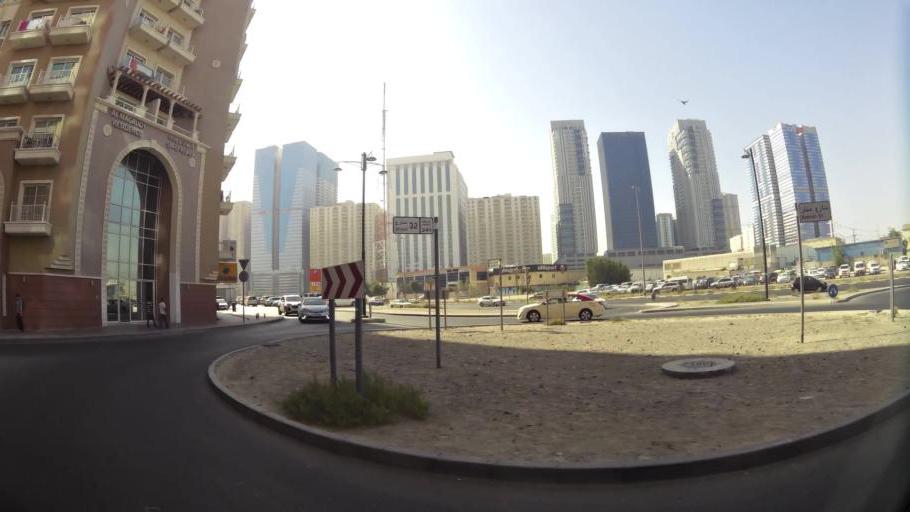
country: AE
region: Ash Shariqah
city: Sharjah
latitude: 25.2975
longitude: 55.3837
